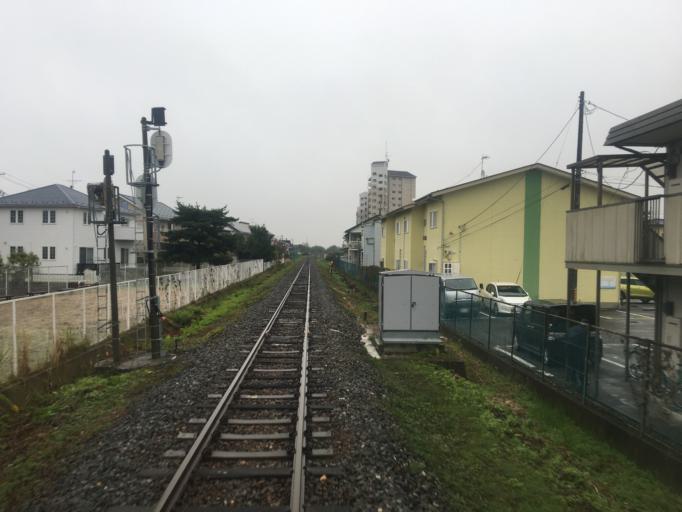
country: JP
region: Miyagi
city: Furukawa
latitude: 38.5704
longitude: 140.9728
